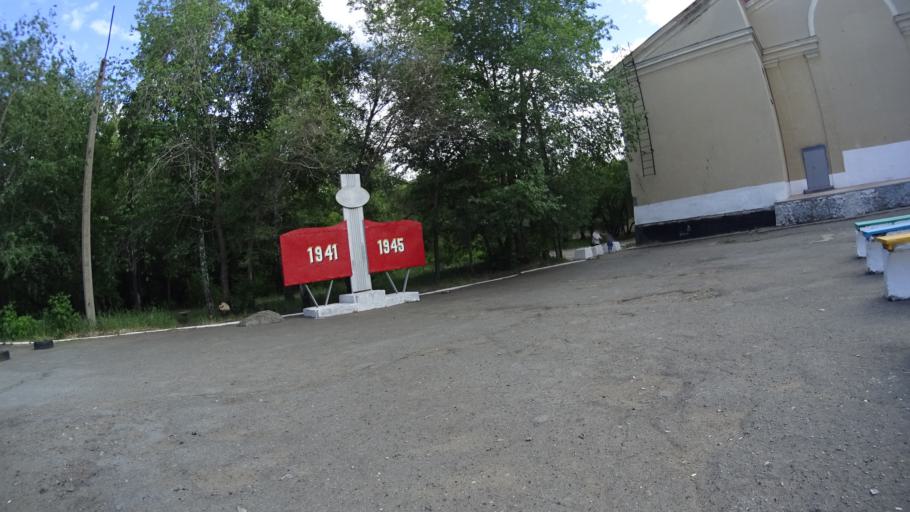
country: RU
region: Chelyabinsk
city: Troitsk
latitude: 54.0468
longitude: 61.6314
